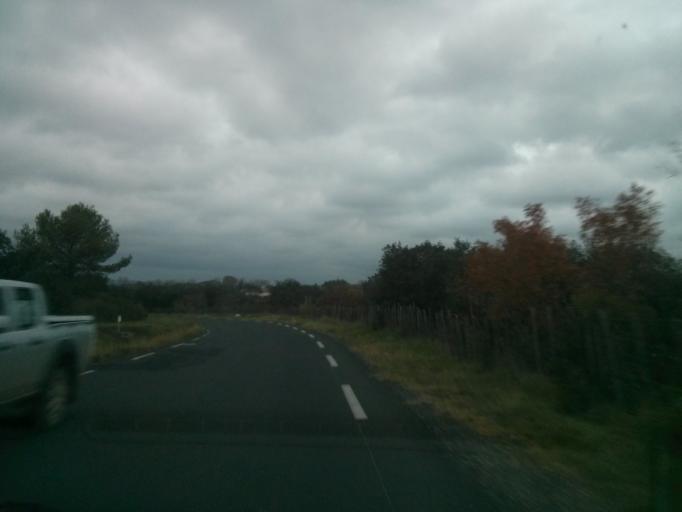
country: FR
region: Languedoc-Roussillon
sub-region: Departement du Gard
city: Aubais
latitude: 43.7517
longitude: 4.1221
